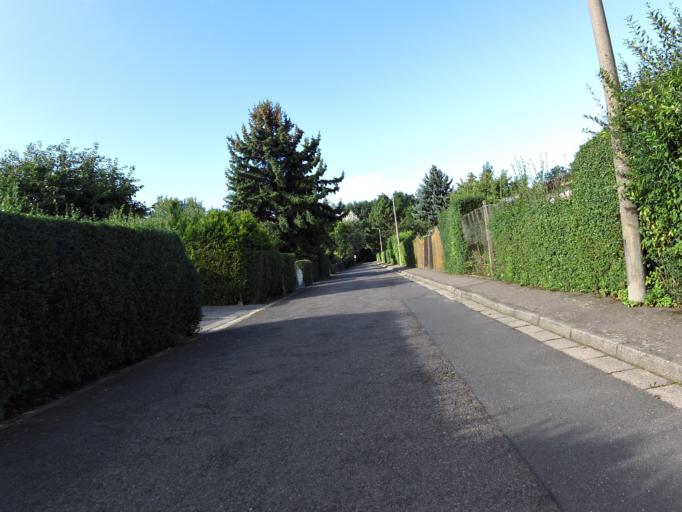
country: DE
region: Saxony
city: Markkleeberg
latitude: 51.2931
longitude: 12.4214
